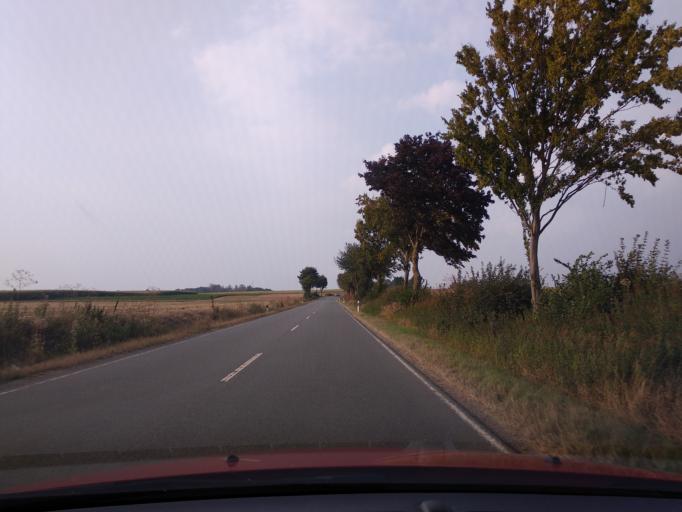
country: DE
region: Hesse
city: Liebenau
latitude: 51.5523
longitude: 9.2970
